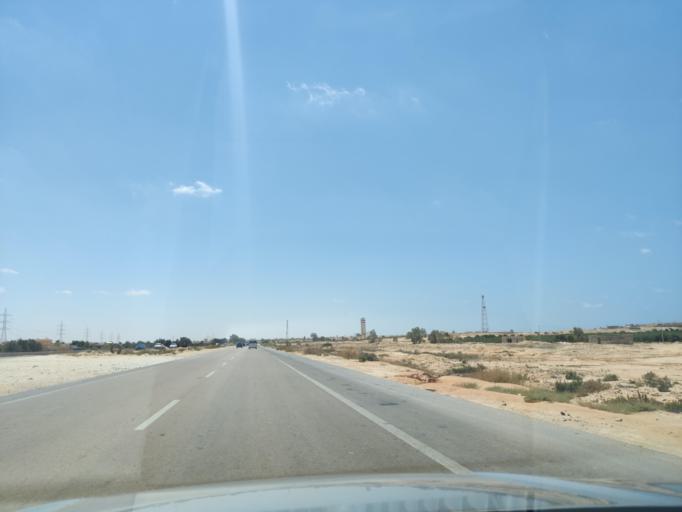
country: EG
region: Muhafazat Matruh
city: Al `Alamayn
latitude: 31.0700
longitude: 28.1482
